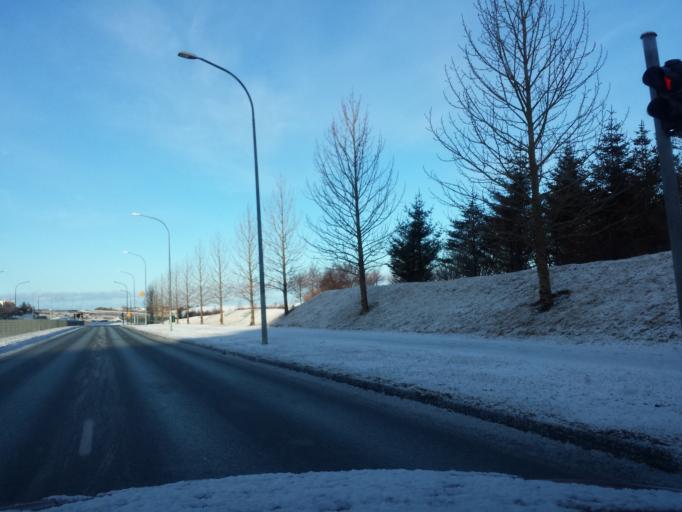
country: IS
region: Capital Region
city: Kopavogur
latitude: 64.1026
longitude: -21.8887
